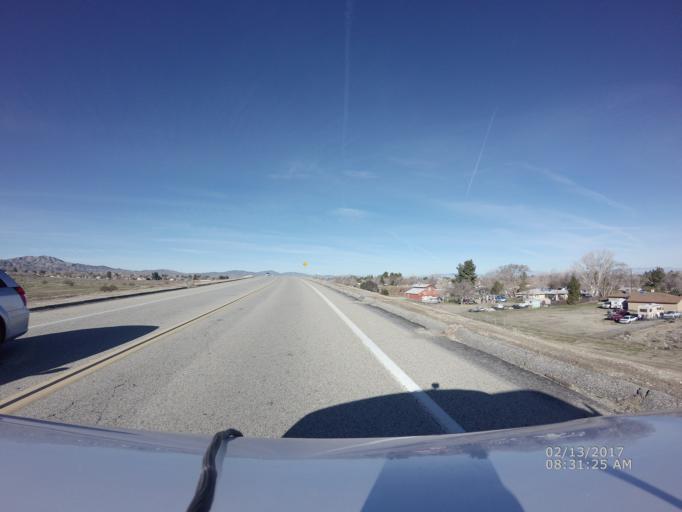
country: US
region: California
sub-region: Los Angeles County
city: Littlerock
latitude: 34.5434
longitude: -117.9514
